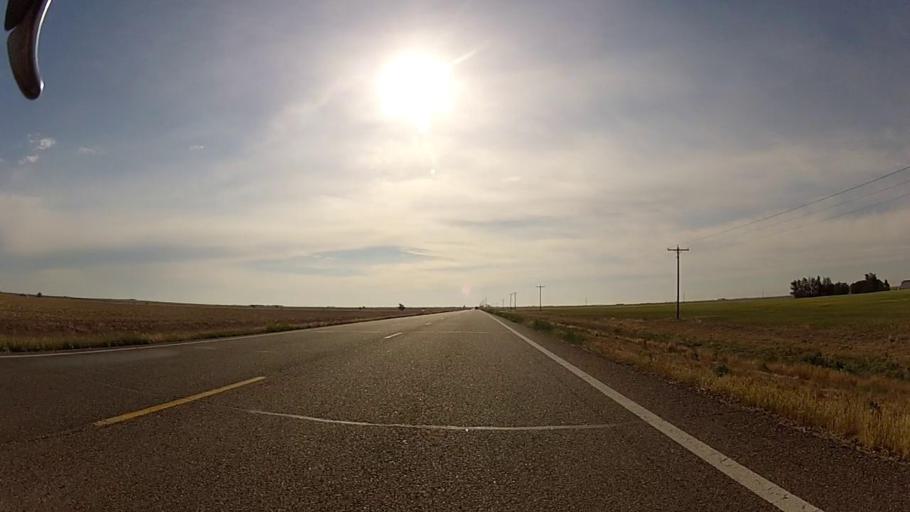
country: US
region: Kansas
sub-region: Grant County
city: Ulysses
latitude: 37.5766
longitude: -101.4471
